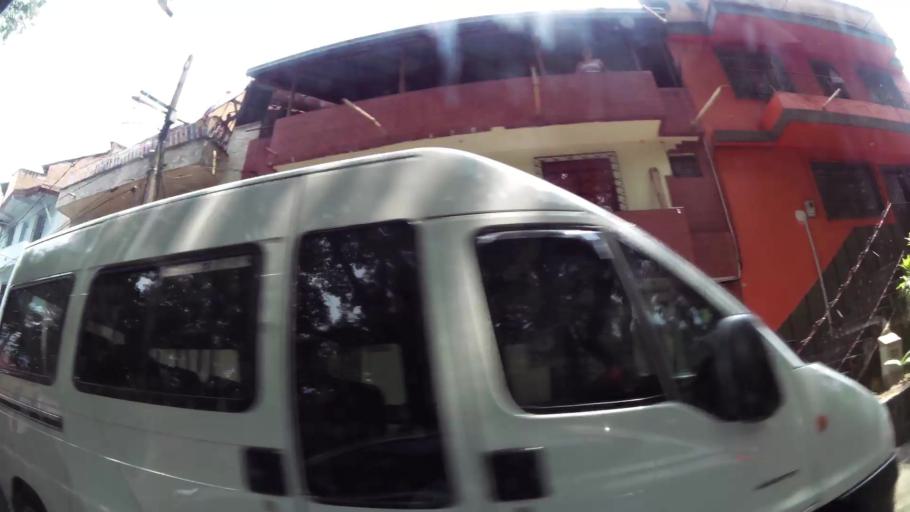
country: CO
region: Antioquia
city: Medellin
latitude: 6.2622
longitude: -75.5499
